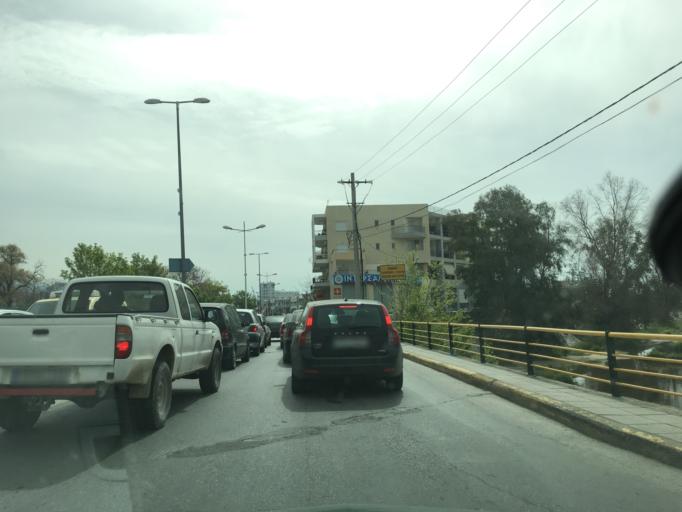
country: GR
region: Thessaly
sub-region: Nomos Magnisias
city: Nea Ionia
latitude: 39.3629
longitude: 22.9313
